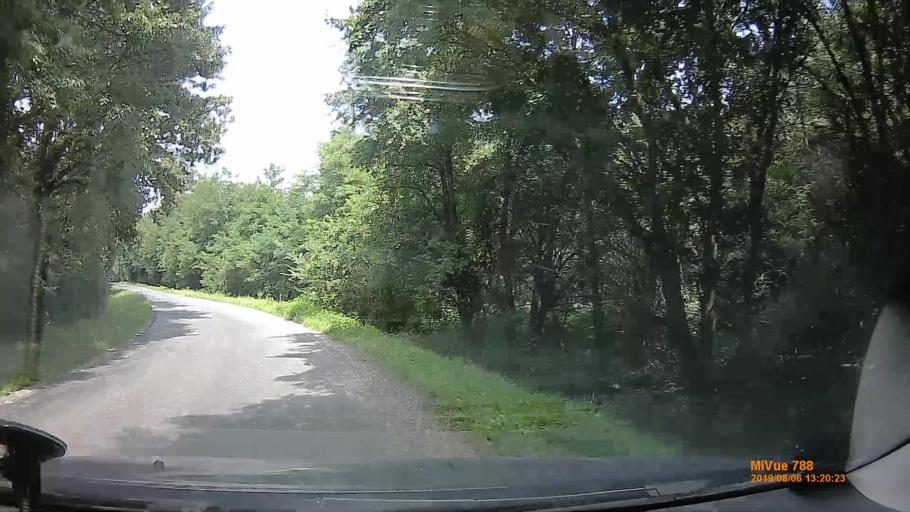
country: HU
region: Zala
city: Pacsa
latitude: 46.6378
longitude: 17.0758
